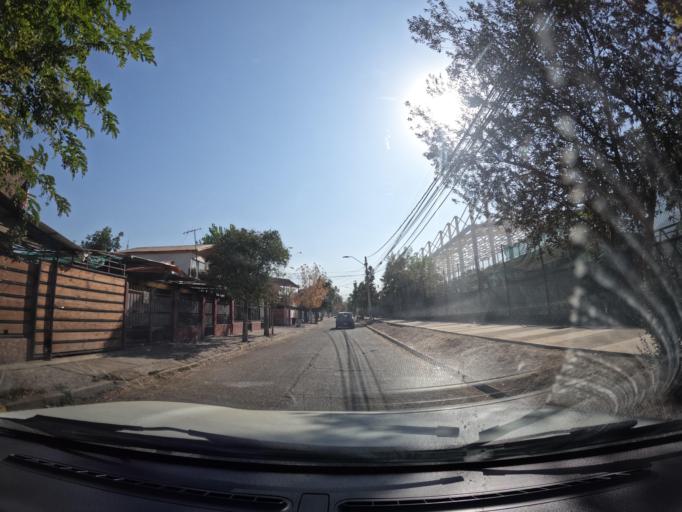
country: CL
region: Santiago Metropolitan
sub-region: Provincia de Santiago
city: Villa Presidente Frei, Nunoa, Santiago, Chile
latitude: -33.4661
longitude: -70.5591
